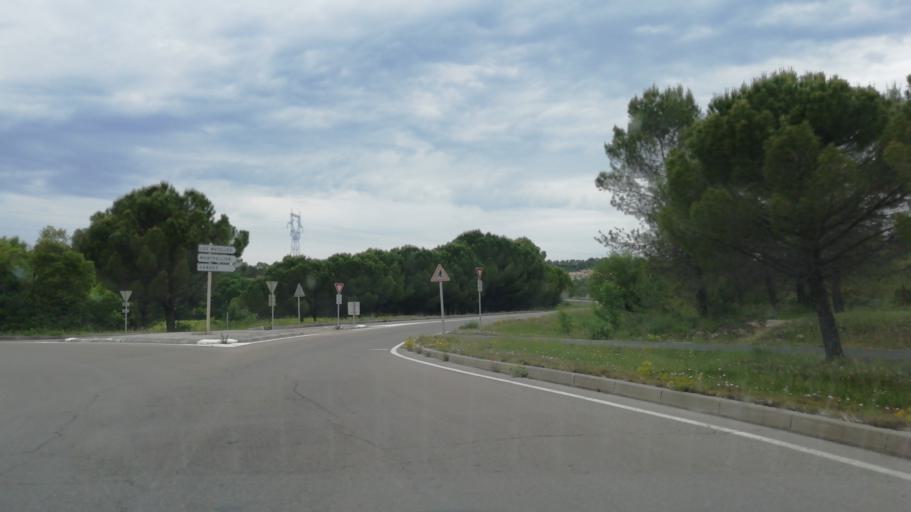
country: FR
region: Languedoc-Roussillon
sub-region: Departement de l'Herault
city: Saint-Gely-du-Fesc
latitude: 43.7069
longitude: 3.8240
